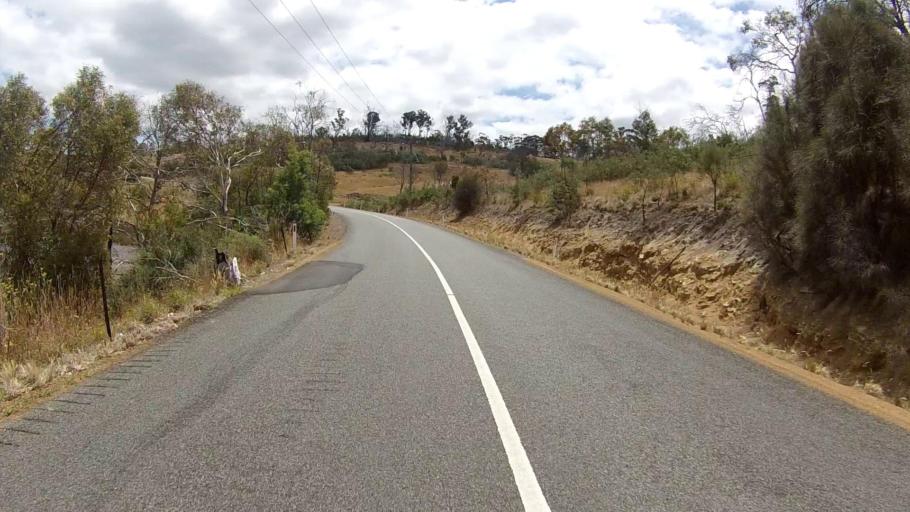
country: AU
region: Tasmania
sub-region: Sorell
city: Sorell
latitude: -42.8642
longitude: 147.6910
